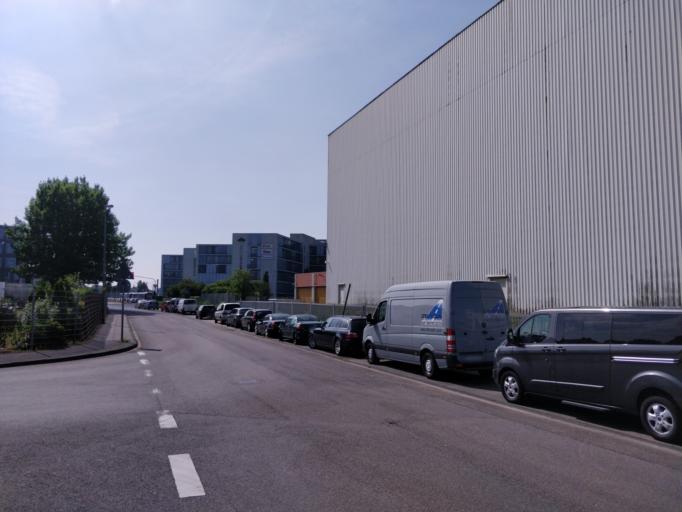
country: DE
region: North Rhine-Westphalia
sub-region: Regierungsbezirk Koln
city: Mengenich
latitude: 50.9862
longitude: 6.8865
